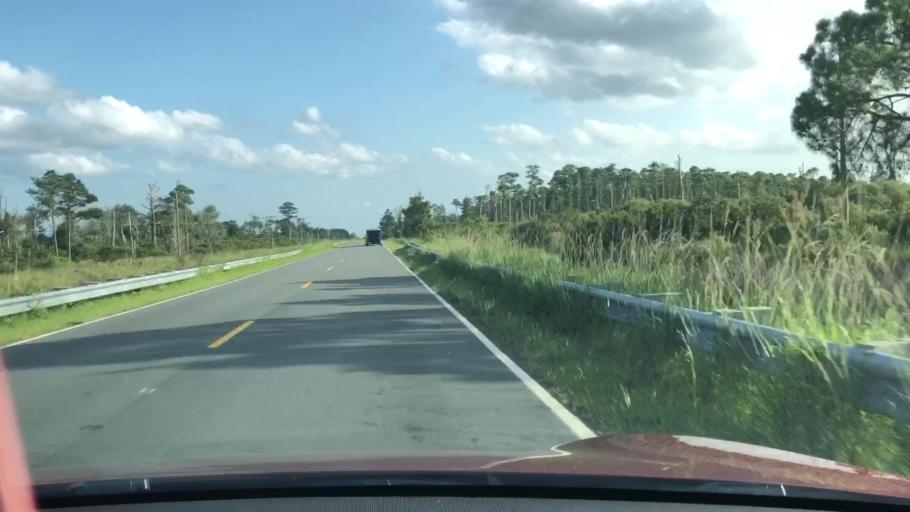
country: US
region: North Carolina
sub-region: Dare County
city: Wanchese
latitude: 35.6836
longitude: -75.7808
